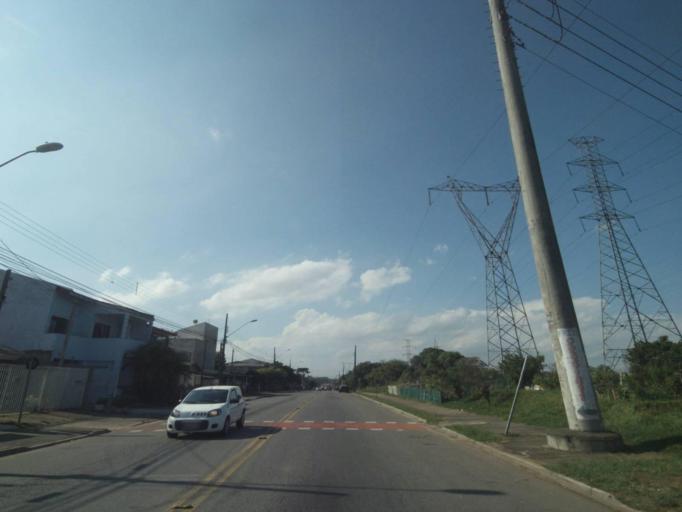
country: BR
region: Parana
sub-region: Araucaria
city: Araucaria
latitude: -25.5303
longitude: -49.3322
